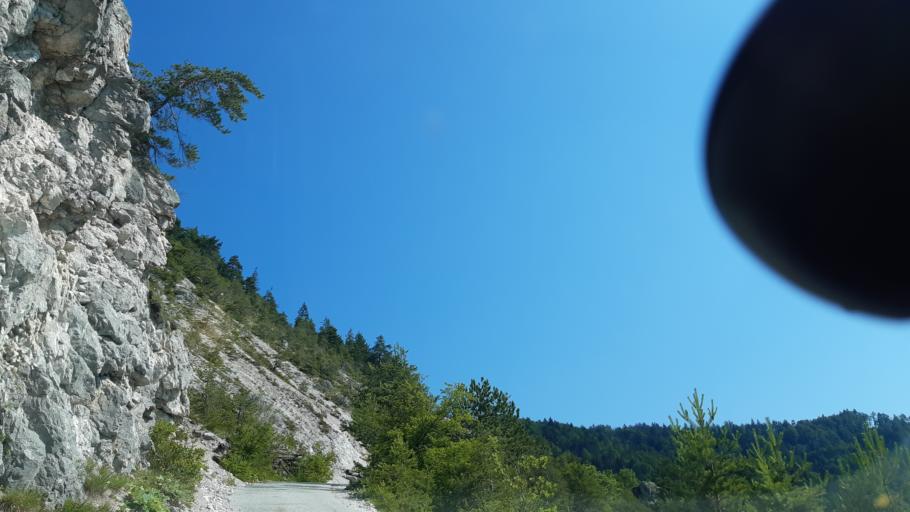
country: SI
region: Trzic
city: Bistrica pri Trzicu
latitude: 46.3627
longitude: 14.2781
